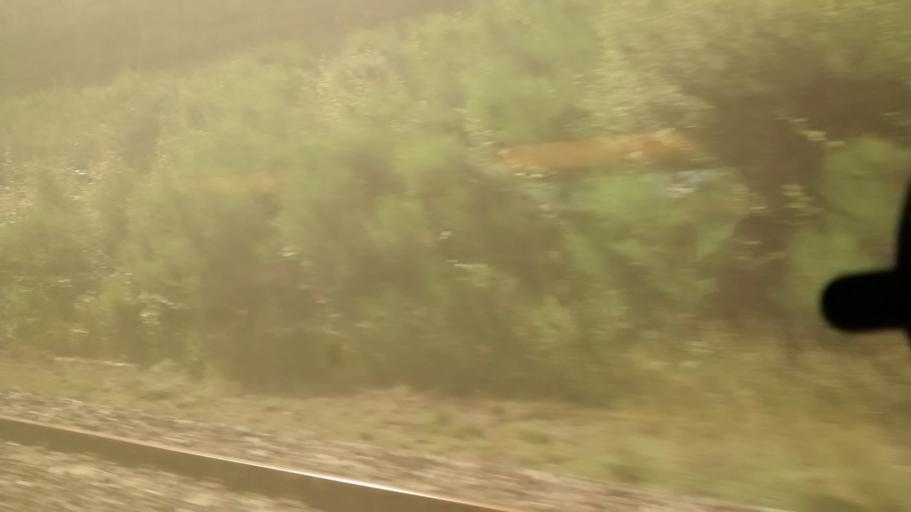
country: FR
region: Pays de la Loire
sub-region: Departement de la Sarthe
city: Le Luart
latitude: 48.0732
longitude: 0.6592
